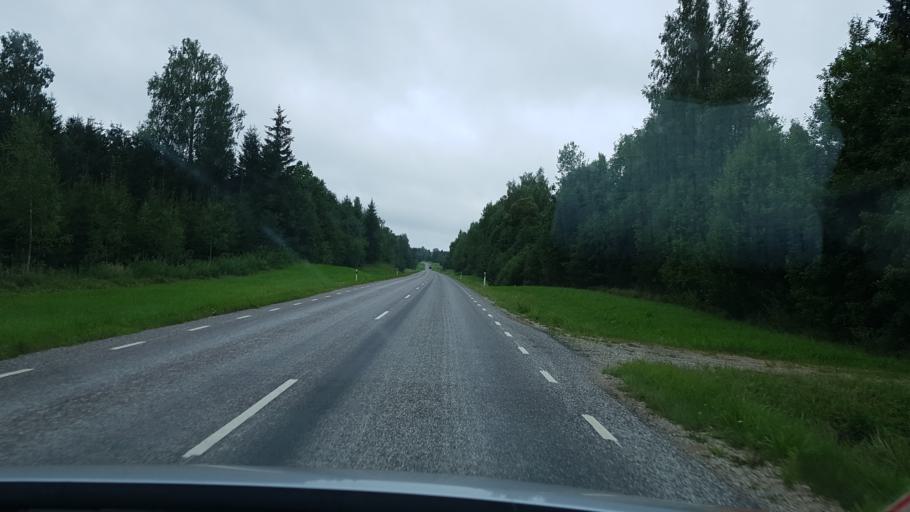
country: EE
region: Vorumaa
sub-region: Antsla vald
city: Vana-Antsla
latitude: 58.0043
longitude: 26.6999
